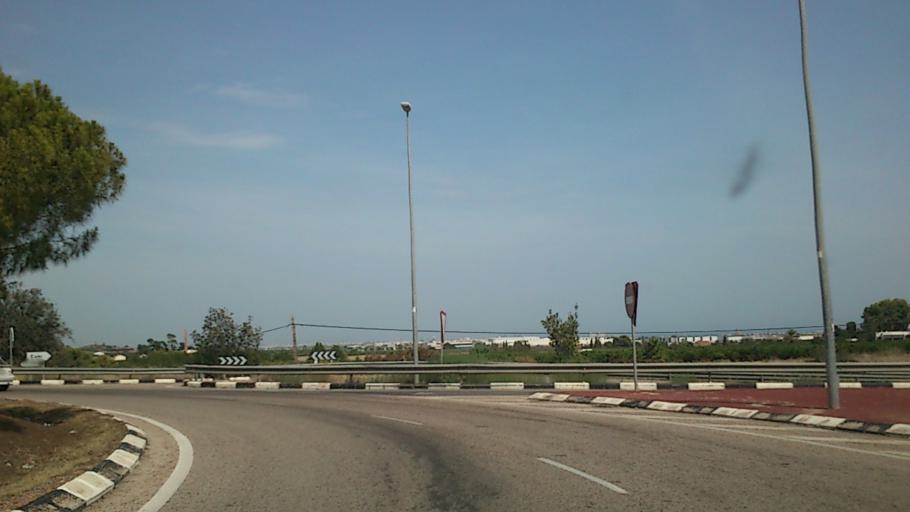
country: ES
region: Valencia
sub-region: Provincia de Valencia
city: Museros
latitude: 39.6082
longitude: -0.3437
